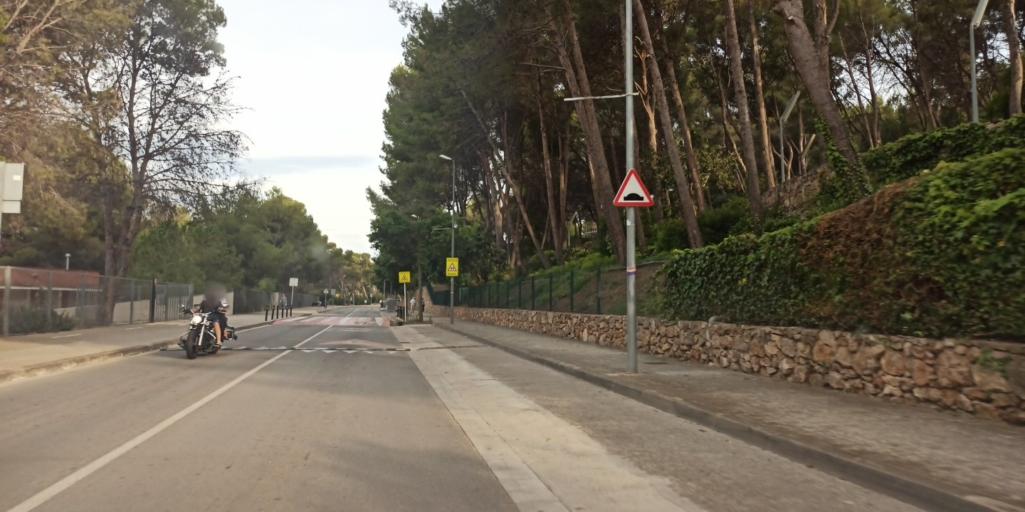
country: ES
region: Catalonia
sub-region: Provincia de Barcelona
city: Castelldefels
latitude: 41.2876
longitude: 1.9728
